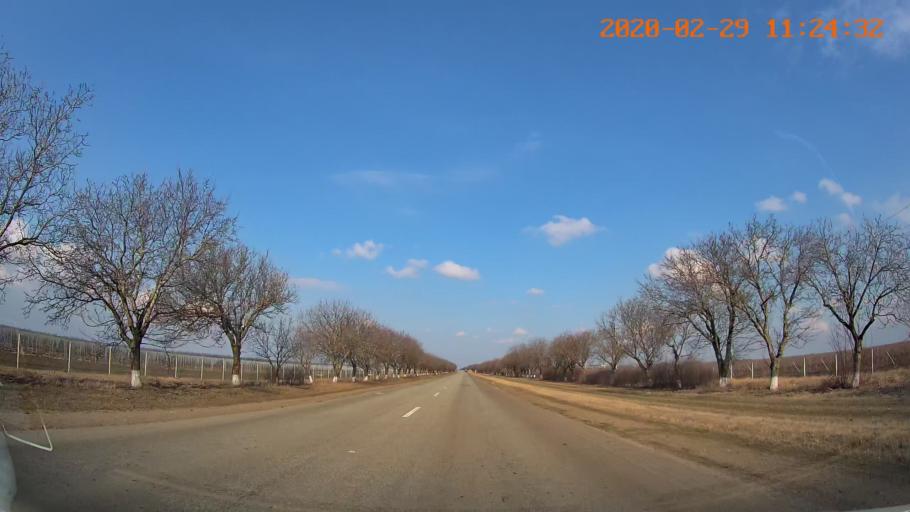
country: MD
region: Telenesti
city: Cocieri
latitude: 47.4253
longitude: 29.1542
